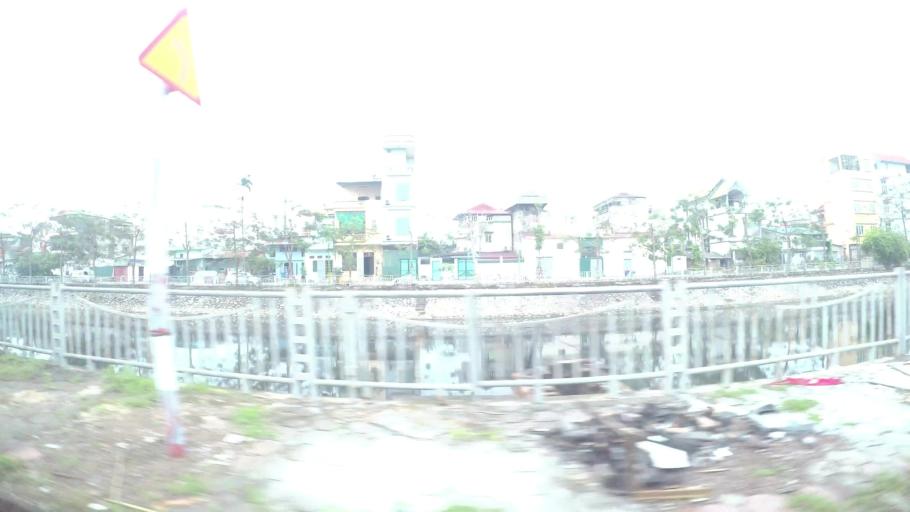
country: VN
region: Ha Noi
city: Van Dien
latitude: 20.9730
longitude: 105.8524
